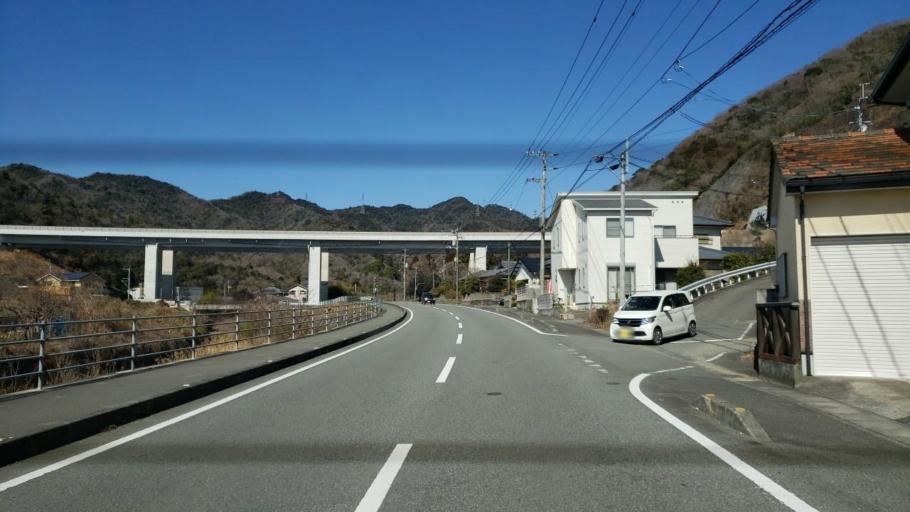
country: JP
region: Tokushima
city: Narutocho-mitsuishi
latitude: 34.1644
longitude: 134.5413
